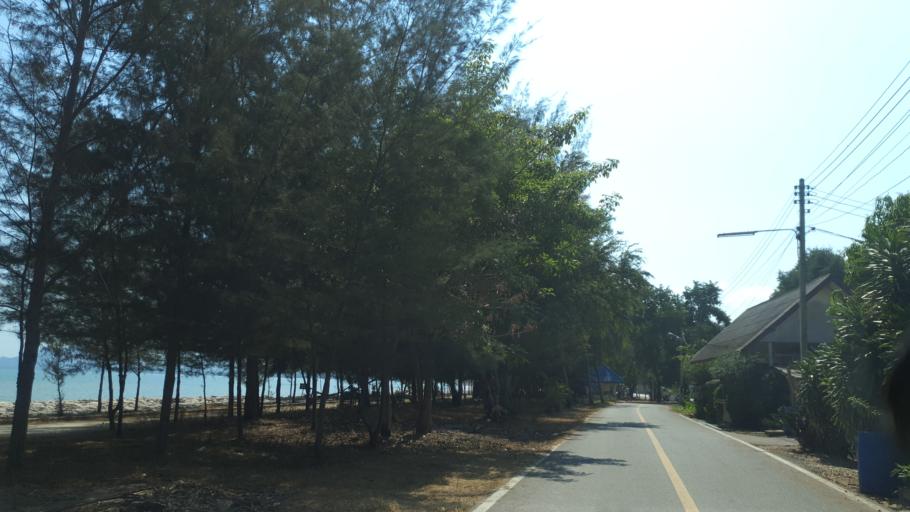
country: TH
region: Prachuap Khiri Khan
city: Sam Roi Yot
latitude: 12.2774
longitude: 99.9745
